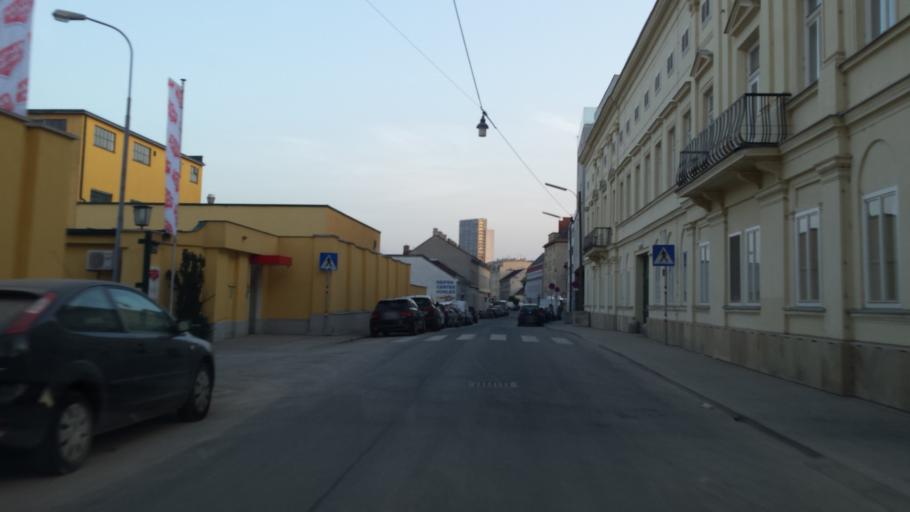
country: AT
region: Vienna
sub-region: Wien Stadt
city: Vienna
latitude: 48.1760
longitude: 16.4205
